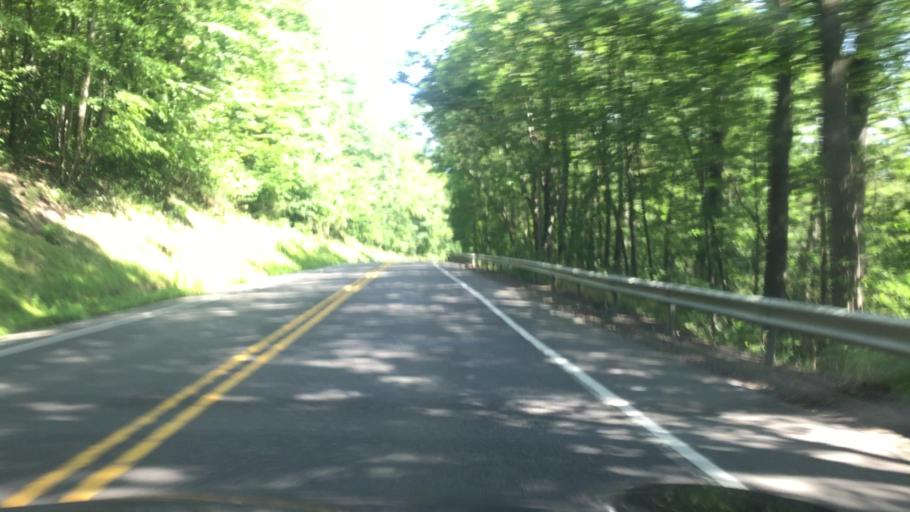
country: US
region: Pennsylvania
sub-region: Lycoming County
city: Garden View
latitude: 41.4065
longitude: -77.0446
